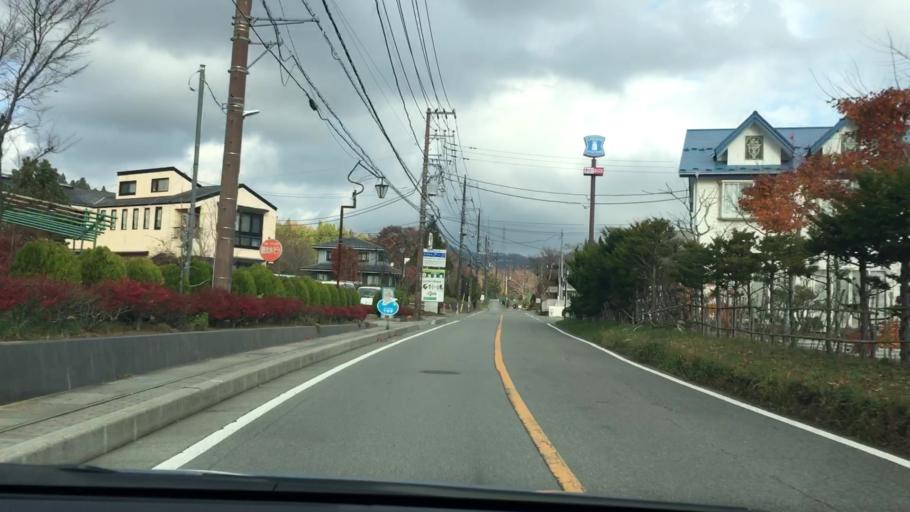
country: JP
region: Shizuoka
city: Gotemba
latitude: 35.4330
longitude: 138.9084
